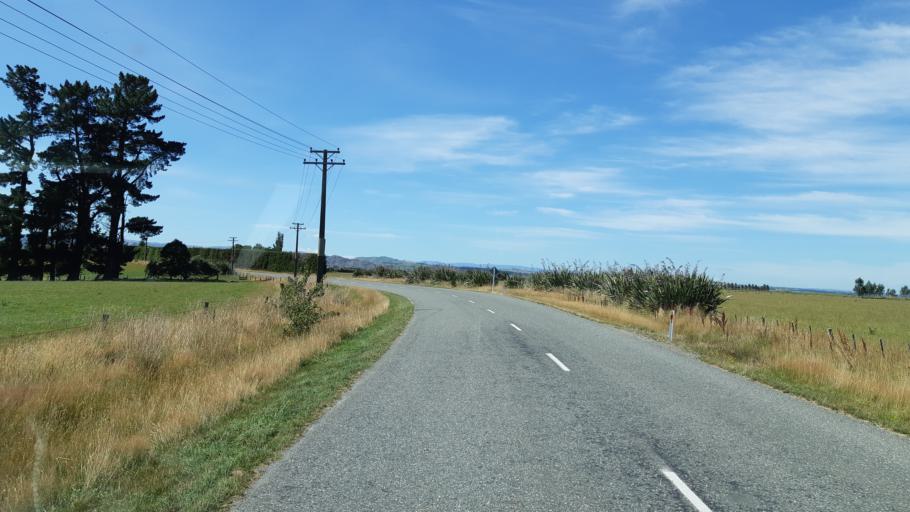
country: NZ
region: Southland
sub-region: Gore District
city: Gore
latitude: -45.9210
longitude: 168.7208
